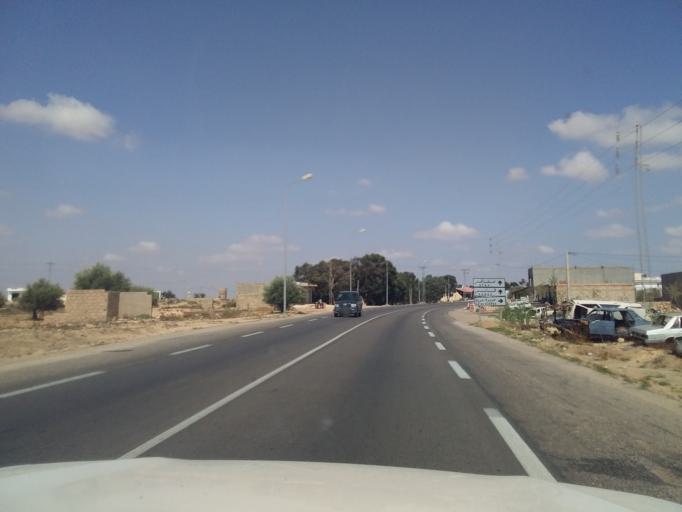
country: TN
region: Madanin
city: Medenine
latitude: 33.5880
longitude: 10.3158
